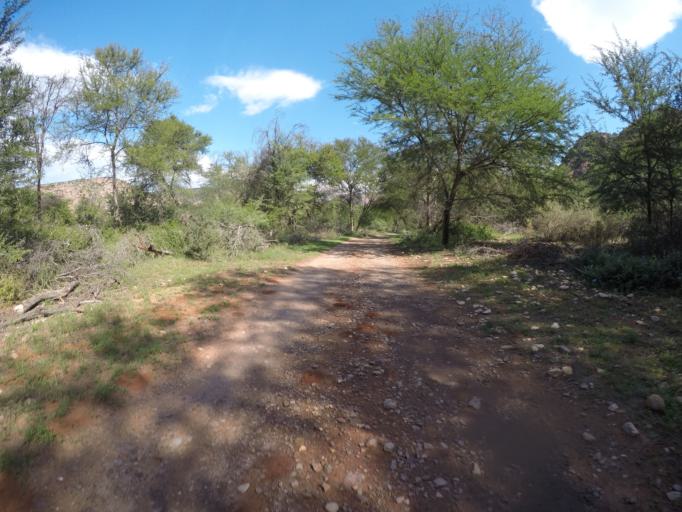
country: ZA
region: Eastern Cape
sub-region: Cacadu District Municipality
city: Kareedouw
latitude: -33.6646
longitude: 24.3884
